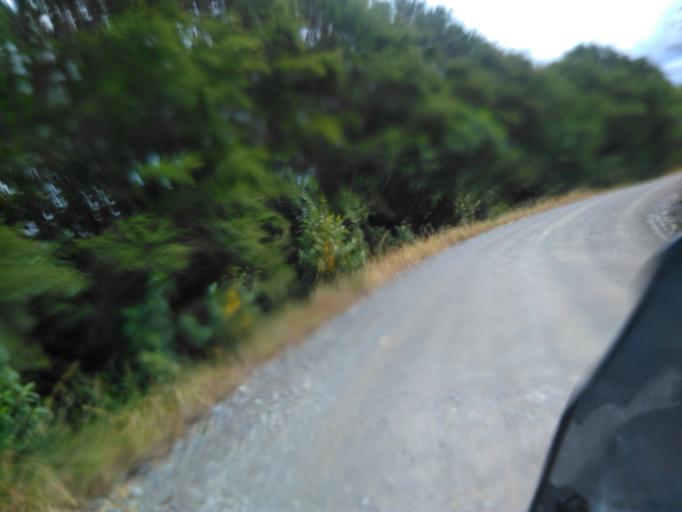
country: NZ
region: Gisborne
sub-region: Gisborne District
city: Gisborne
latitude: -38.1732
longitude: 178.1336
